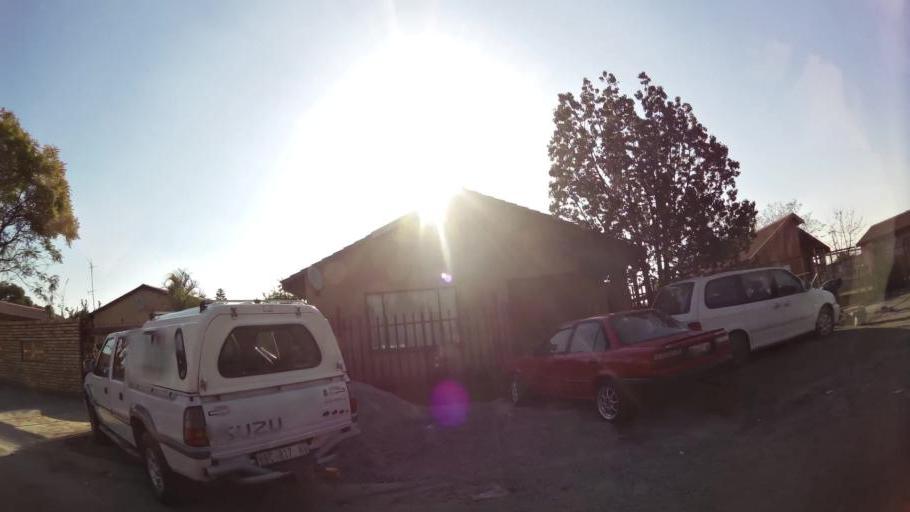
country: ZA
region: North-West
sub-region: Bojanala Platinum District Municipality
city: Rustenburg
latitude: -25.6417
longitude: 27.2372
